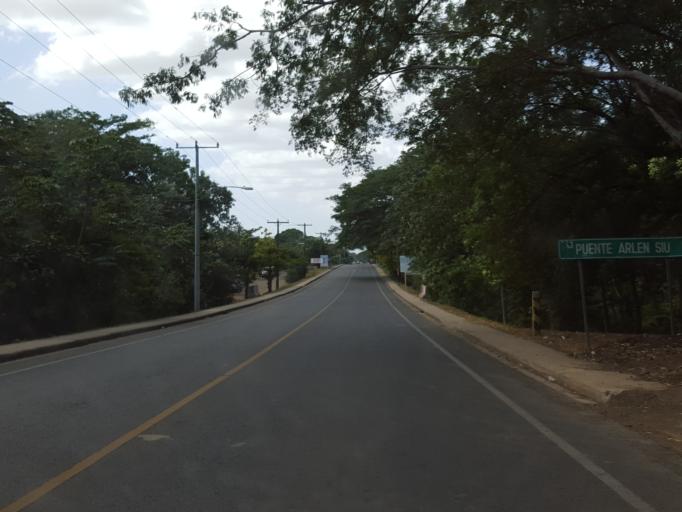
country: NI
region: Leon
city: Leon
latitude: 12.4331
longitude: -86.9060
